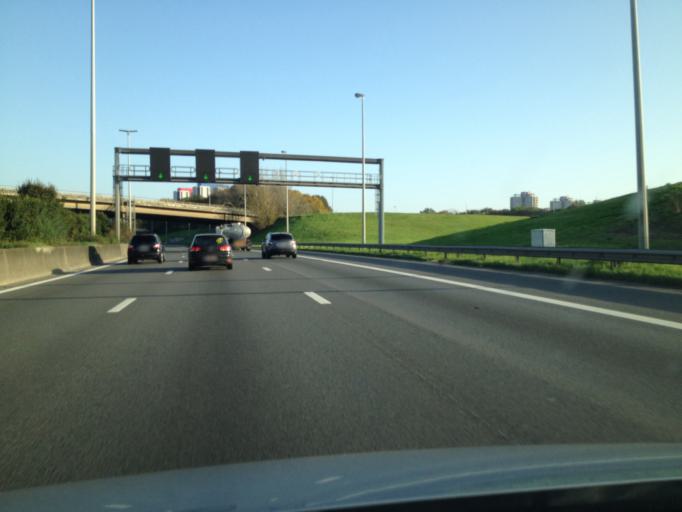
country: BE
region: Flanders
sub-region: Provincie Antwerpen
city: Antwerpen
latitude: 51.1993
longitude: 4.3791
